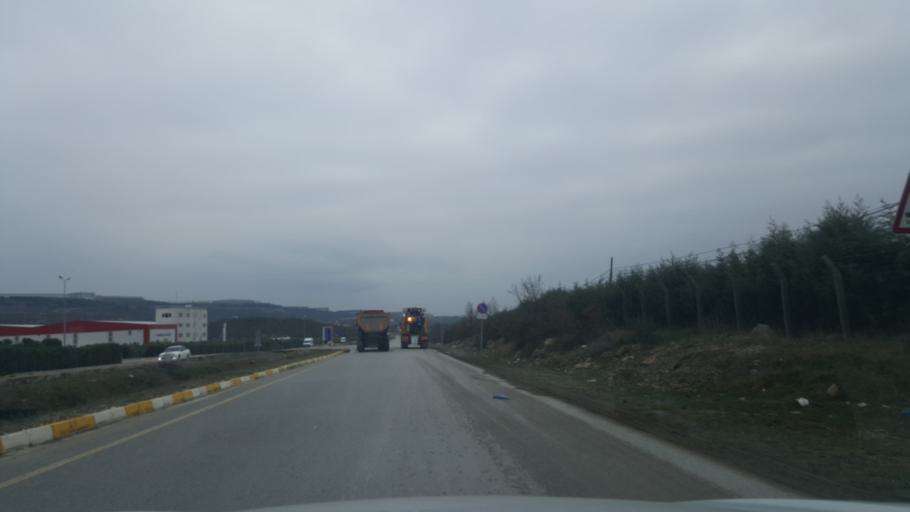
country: TR
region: Kocaeli
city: Tavsanli
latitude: 40.8617
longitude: 29.5584
